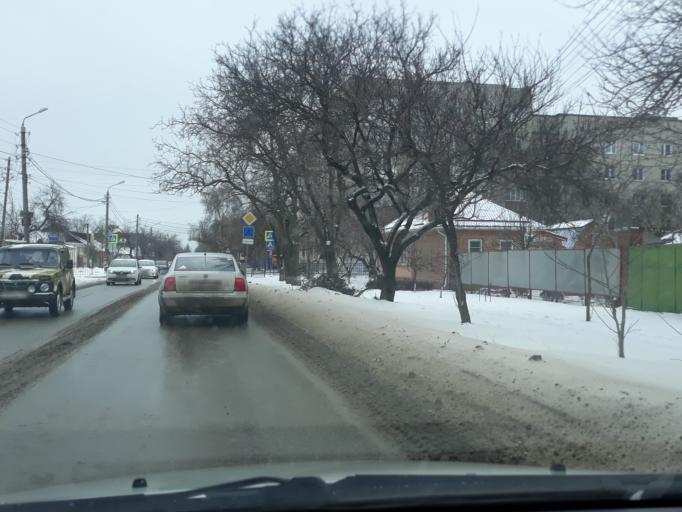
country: RU
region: Rostov
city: Taganrog
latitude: 47.2438
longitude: 38.8771
